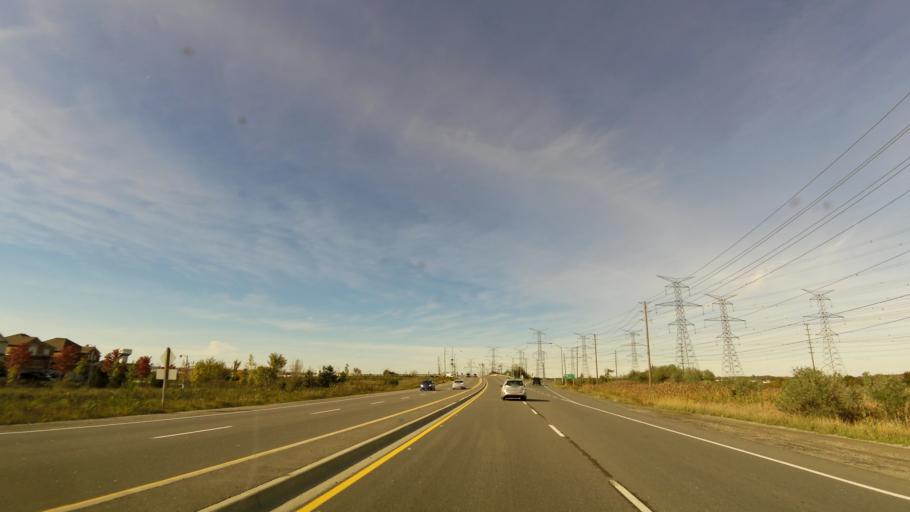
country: CA
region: Ontario
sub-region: Halton
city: Milton
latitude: 43.5398
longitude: -79.8587
